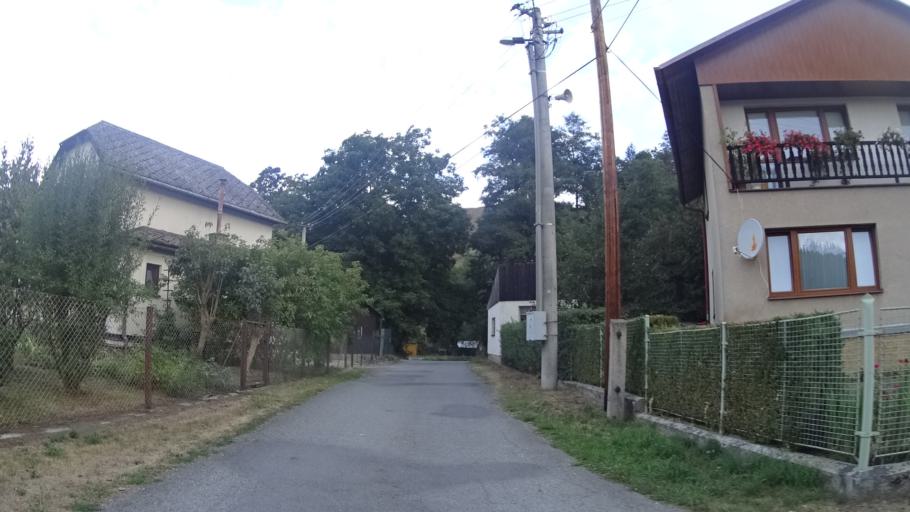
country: CZ
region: Olomoucky
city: Stity
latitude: 49.8753
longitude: 16.7795
